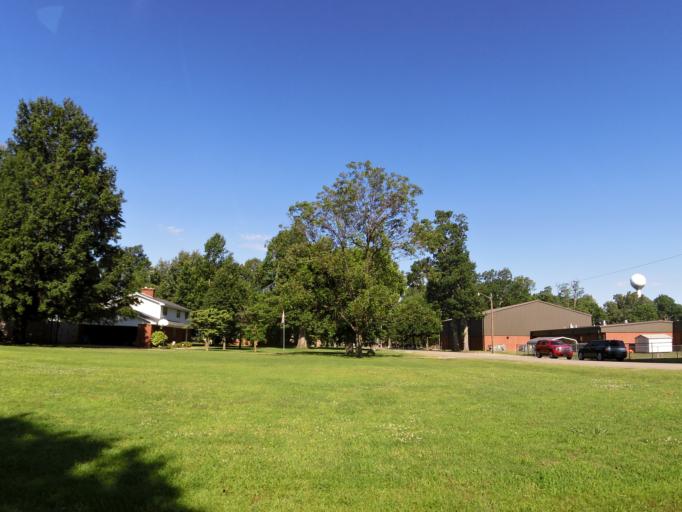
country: US
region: Arkansas
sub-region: Clay County
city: Corning
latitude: 36.4086
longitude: -90.5921
